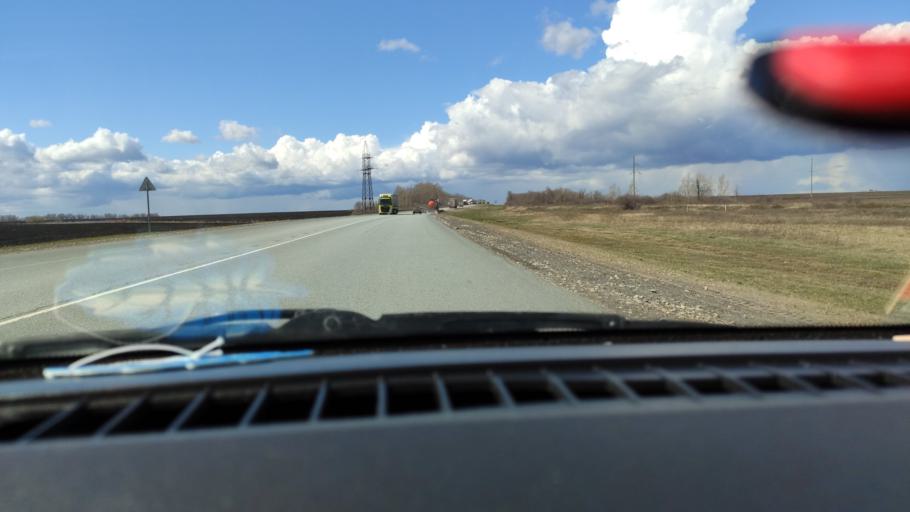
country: RU
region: Samara
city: Obsharovka
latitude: 53.2134
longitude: 48.7721
